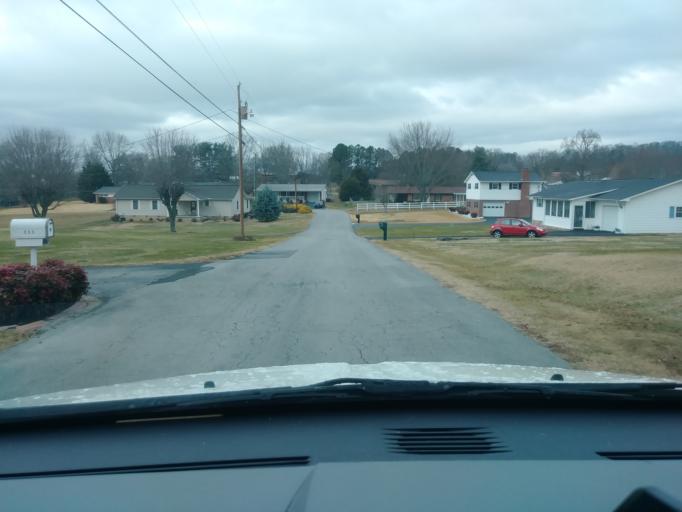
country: US
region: Tennessee
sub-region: Greene County
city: Greeneville
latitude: 36.1376
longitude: -82.8516
